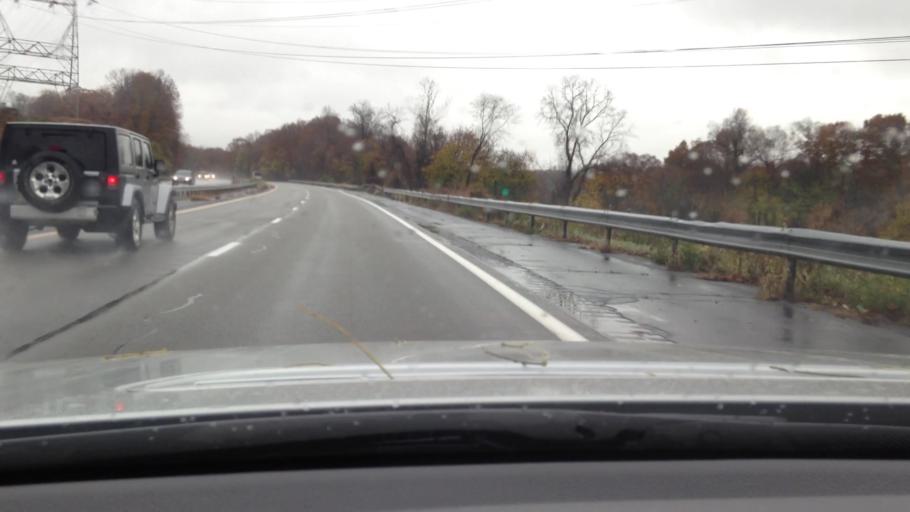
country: US
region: New York
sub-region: Westchester County
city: Montrose
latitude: 41.2544
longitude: -73.9283
